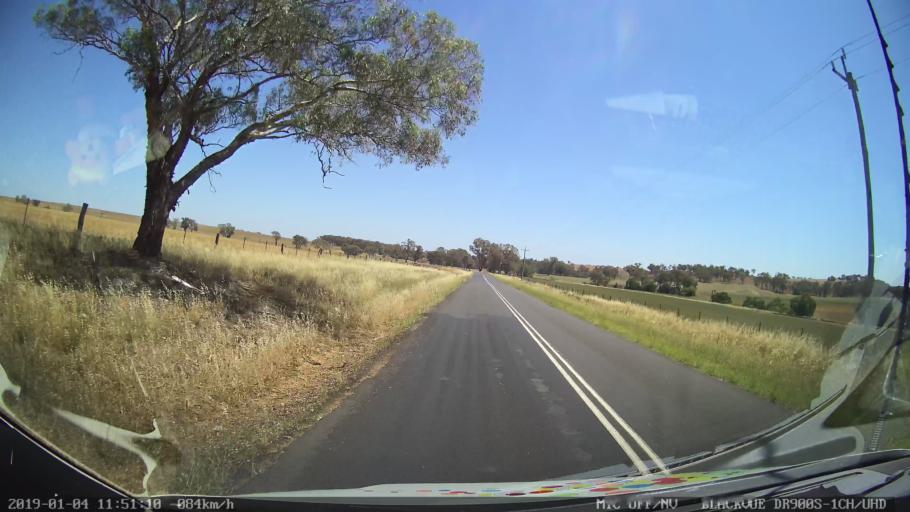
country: AU
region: New South Wales
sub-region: Cabonne
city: Molong
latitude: -32.8977
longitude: 148.7575
